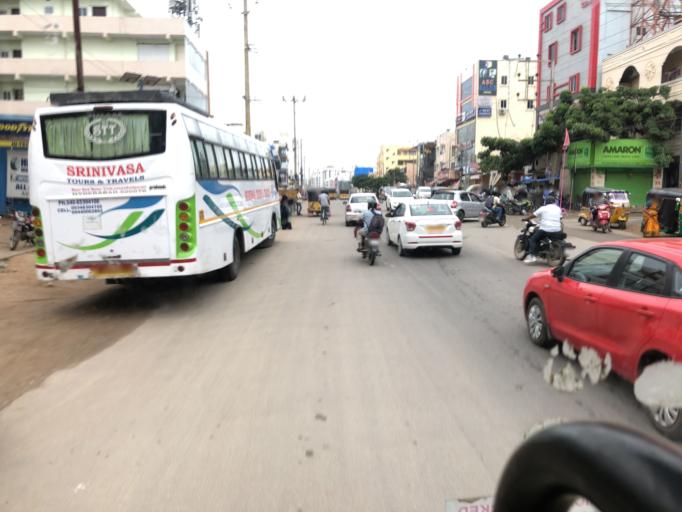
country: IN
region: Telangana
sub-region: Medak
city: Serilingampalle
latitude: 17.4600
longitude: 78.3549
